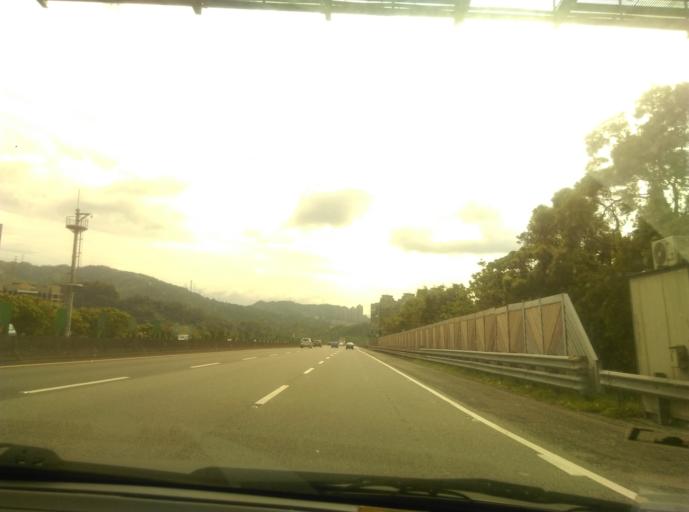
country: TW
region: Taipei
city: Taipei
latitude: 25.0658
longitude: 121.6434
